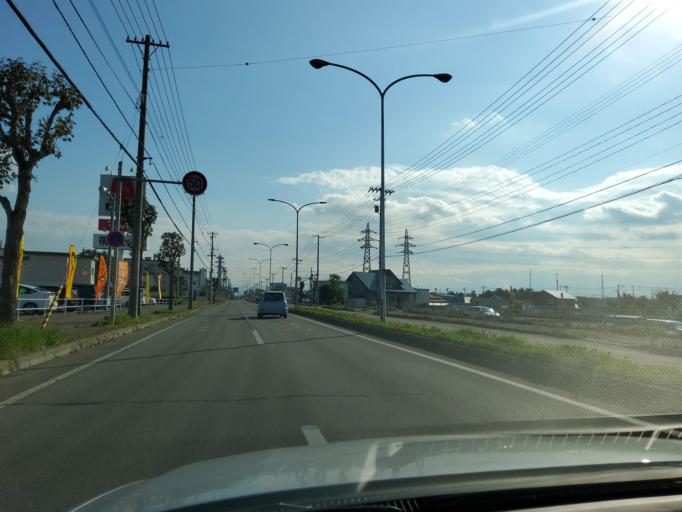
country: JP
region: Hokkaido
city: Obihiro
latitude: 42.8960
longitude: 143.2083
